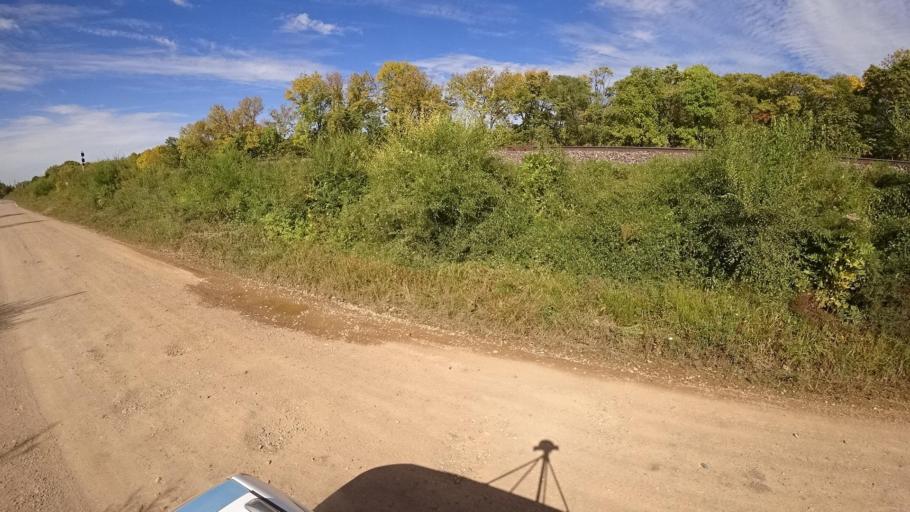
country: RU
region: Primorskiy
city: Yakovlevka
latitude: 44.3916
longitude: 133.6088
